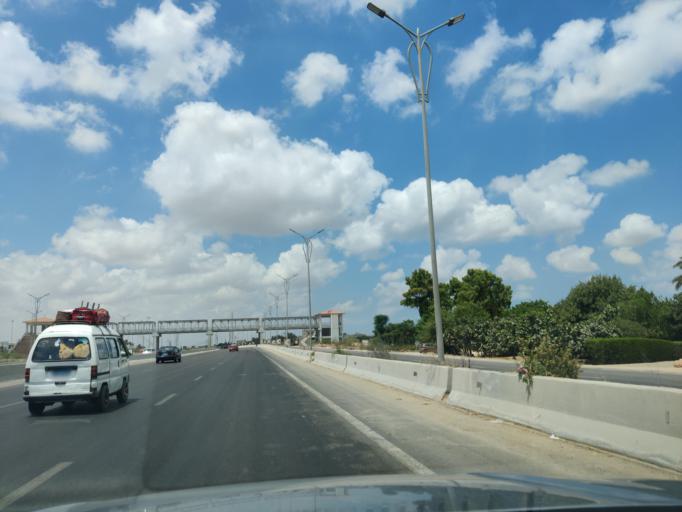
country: EG
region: Alexandria
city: Alexandria
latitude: 31.0071
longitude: 29.7361
